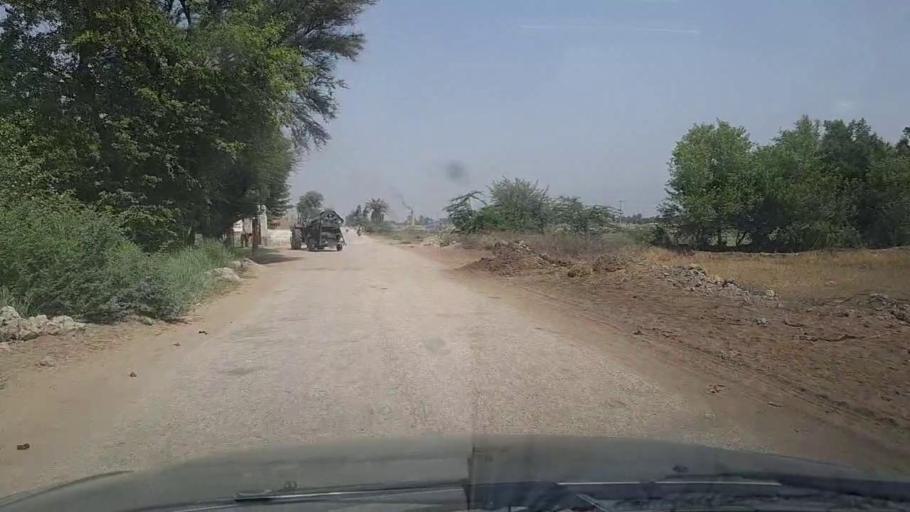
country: PK
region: Sindh
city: Setharja Old
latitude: 27.1444
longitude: 68.5261
